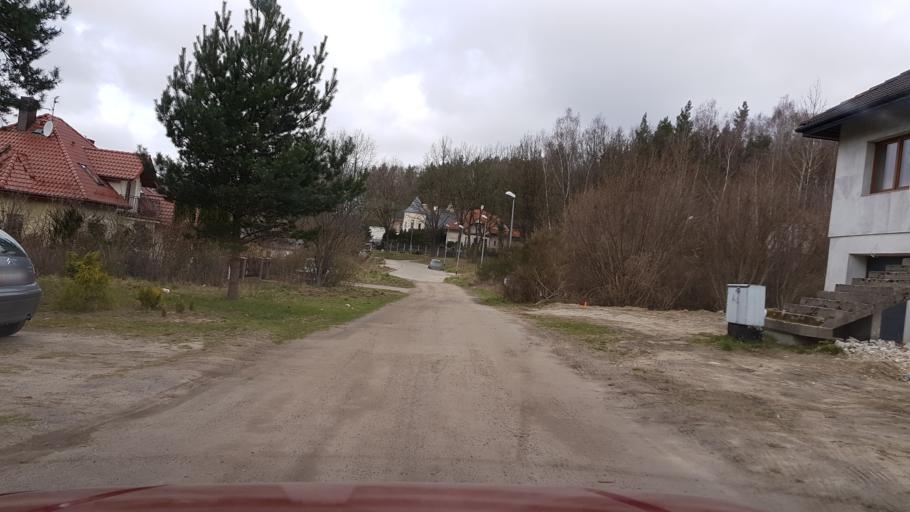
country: PL
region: West Pomeranian Voivodeship
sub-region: Powiat koszalinski
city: Sianow
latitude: 54.1893
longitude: 16.2440
